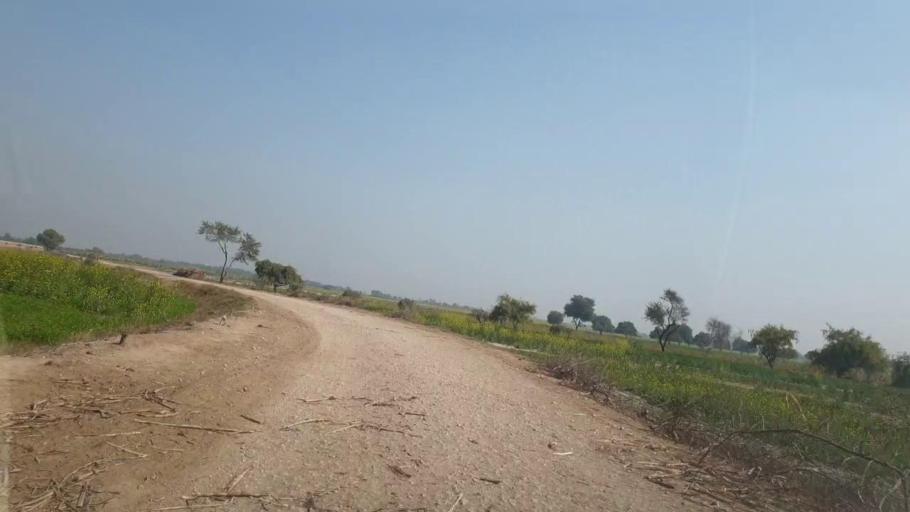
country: PK
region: Sindh
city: Matiari
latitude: 25.5351
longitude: 68.4703
